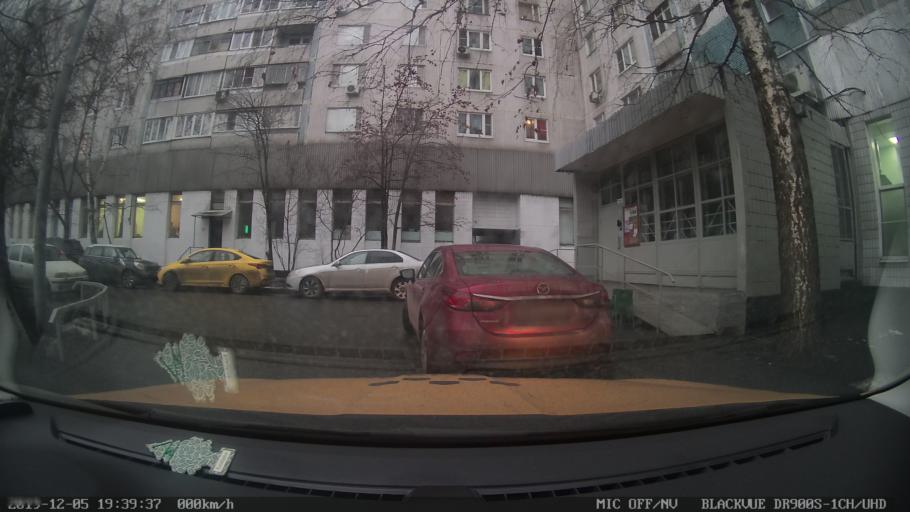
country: RU
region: Moscow
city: Lianozovo
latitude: 55.8972
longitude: 37.5852
